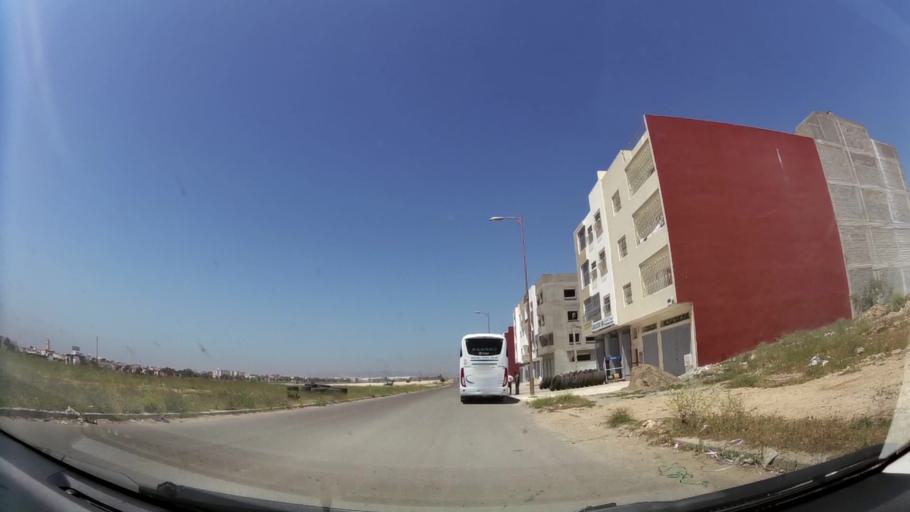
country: MA
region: Oued ed Dahab-Lagouira
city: Dakhla
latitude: 30.4253
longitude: -9.5539
